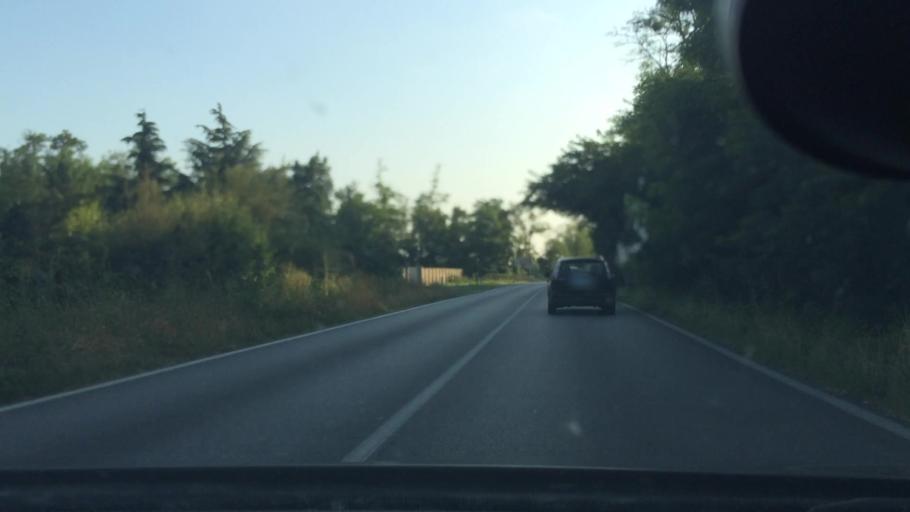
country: IT
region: Lombardy
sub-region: Citta metropolitana di Milano
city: Mantegazza
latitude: 45.5238
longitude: 8.9680
